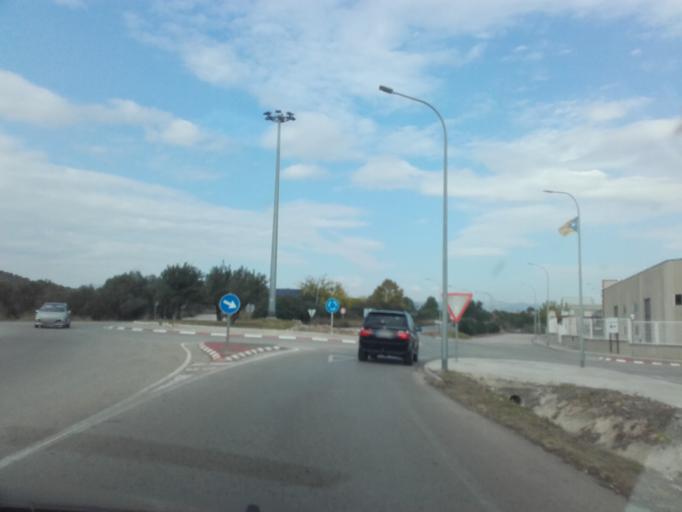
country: ES
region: Catalonia
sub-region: Provincia de Tarragona
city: El Vendrell
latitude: 41.2320
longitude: 1.5287
